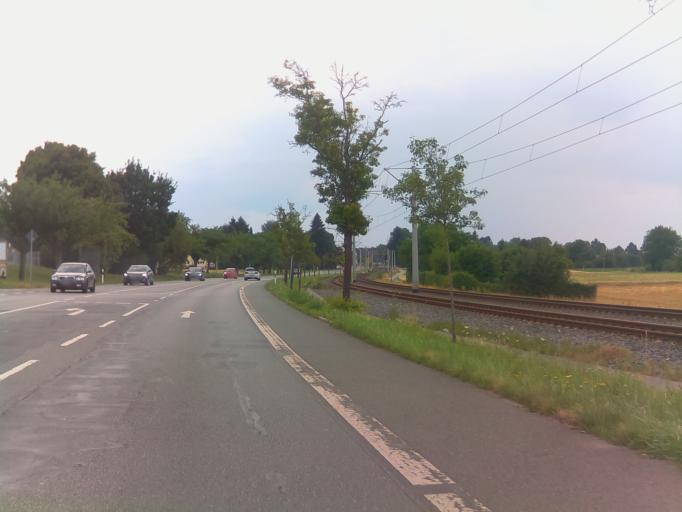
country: DE
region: Hesse
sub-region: Regierungsbezirk Darmstadt
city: Seeheim-Jugenheim
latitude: 49.7611
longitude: 8.6424
